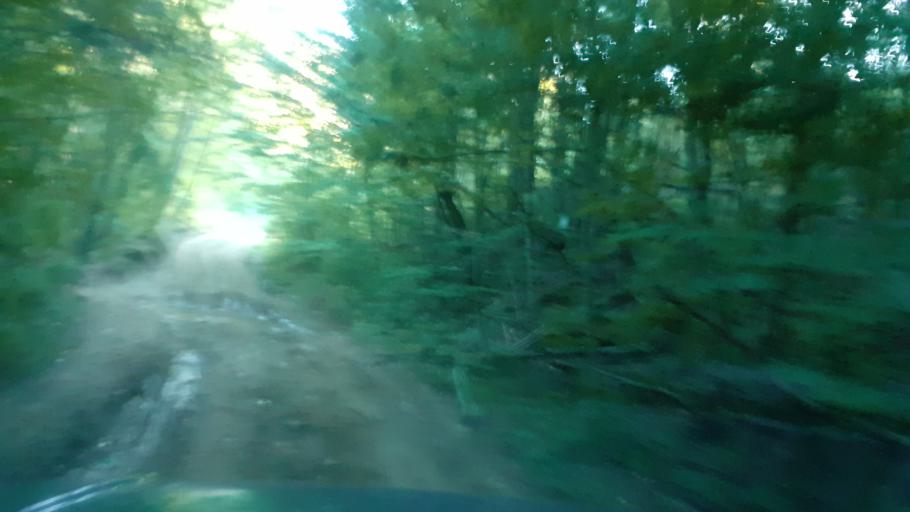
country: RU
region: Krasnodarskiy
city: Pshada
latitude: 44.6569
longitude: 38.4575
